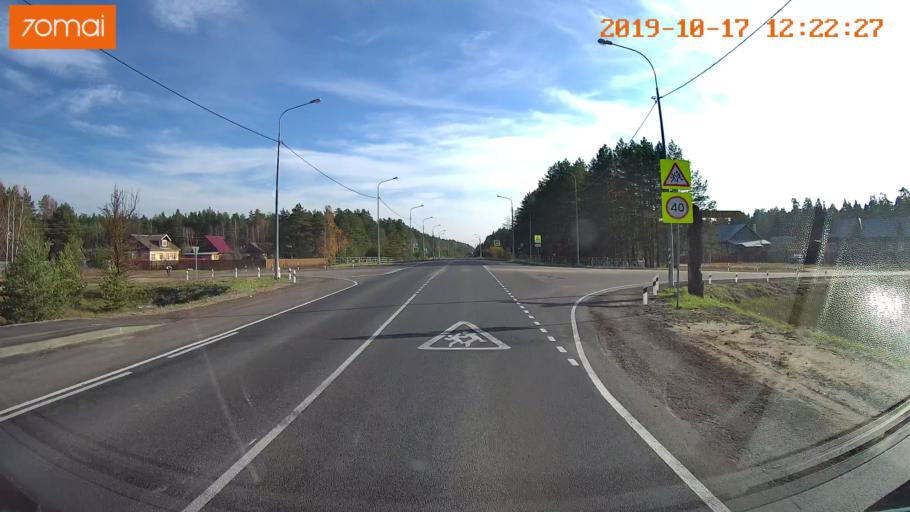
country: RU
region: Rjazan
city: Gus'-Zheleznyy
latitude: 55.0520
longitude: 41.1721
